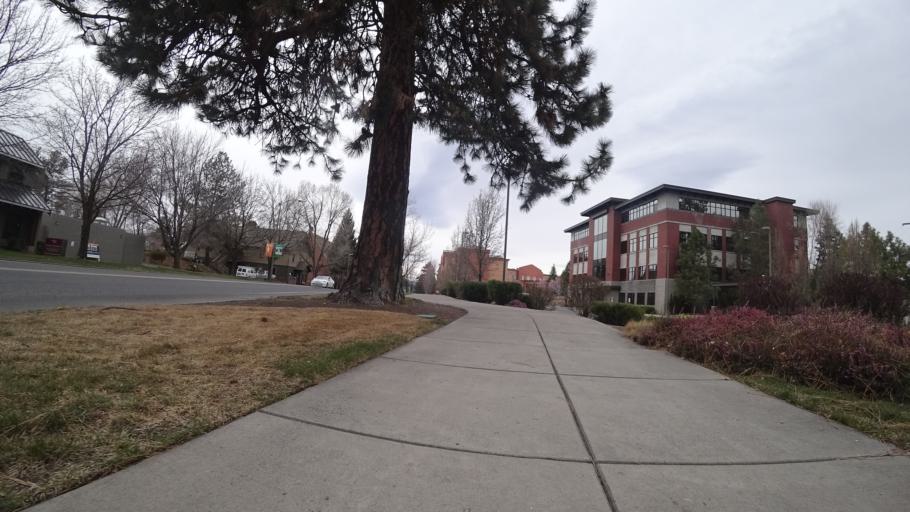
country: US
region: Oregon
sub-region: Deschutes County
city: Bend
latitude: 44.0560
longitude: -121.3100
